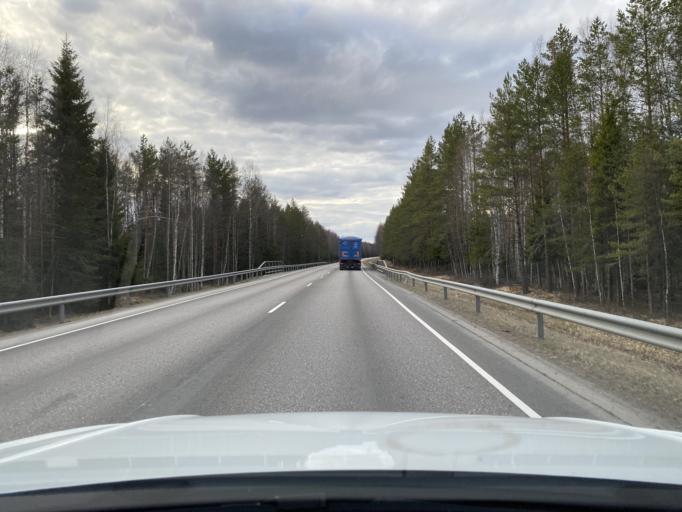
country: FI
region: Uusimaa
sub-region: Helsinki
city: Kaerkoelae
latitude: 60.8105
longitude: 24.0584
